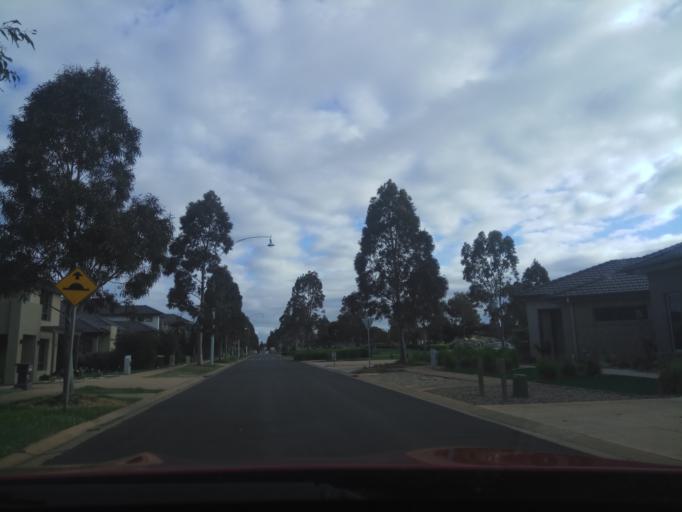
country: AU
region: Victoria
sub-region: Wyndham
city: Point Cook
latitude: -37.9038
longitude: 144.7710
